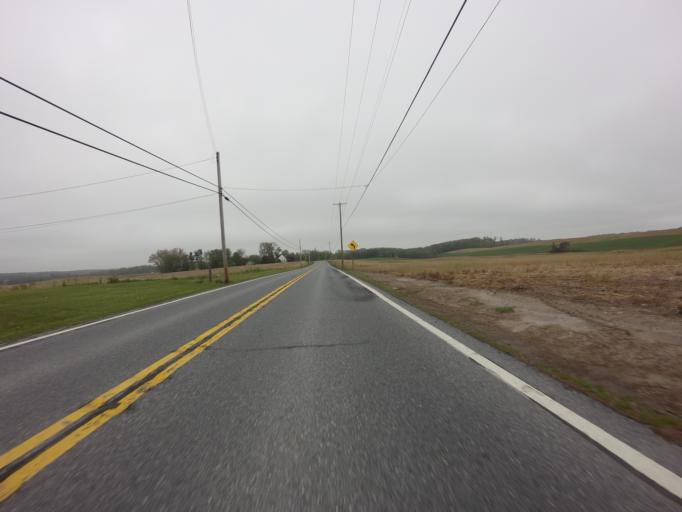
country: US
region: Maryland
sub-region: Baltimore County
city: Hunt Valley
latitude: 39.5845
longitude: -76.7140
